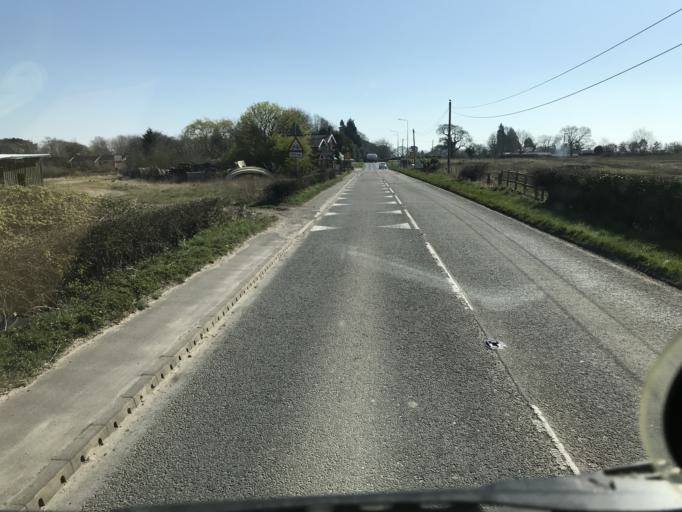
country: GB
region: England
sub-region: Cheshire East
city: Mobberley
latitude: 53.2740
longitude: -2.2922
